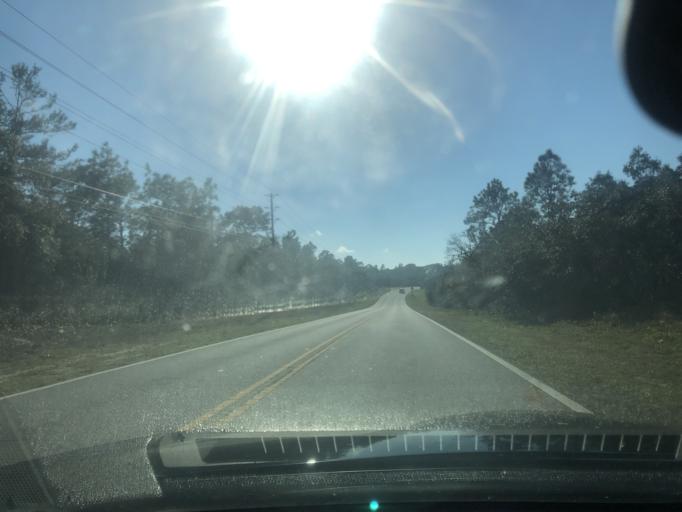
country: US
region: Florida
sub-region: Citrus County
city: Homosassa Springs
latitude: 28.8212
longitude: -82.5315
